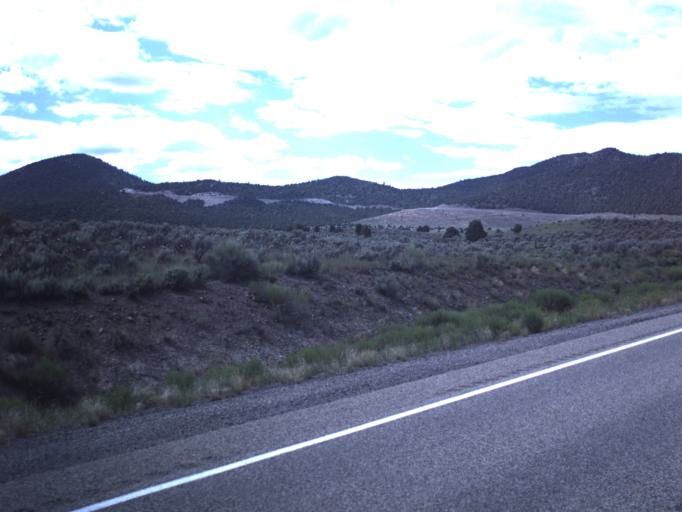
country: US
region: Utah
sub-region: Garfield County
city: Panguitch
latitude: 38.0108
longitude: -112.5089
